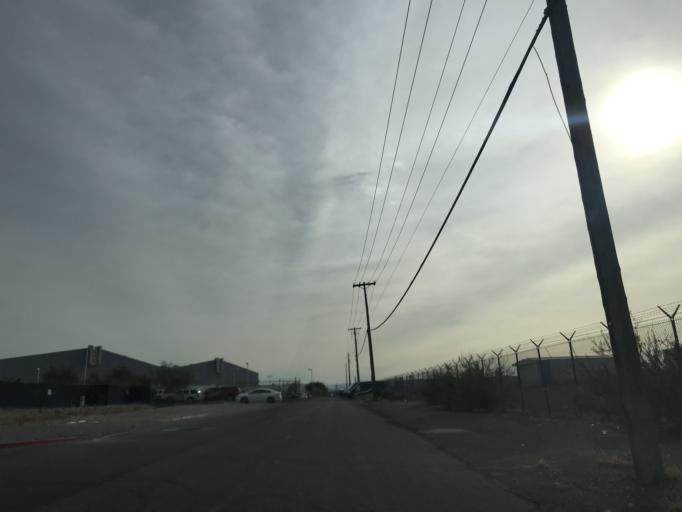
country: US
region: Nevada
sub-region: Clark County
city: Paradise
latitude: 36.0890
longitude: -115.1682
